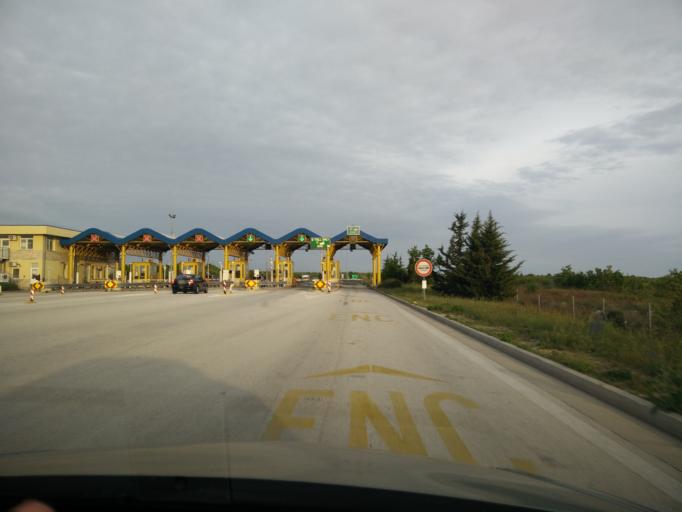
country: HR
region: Zadarska
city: Galovac
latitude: 44.1150
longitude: 15.4362
